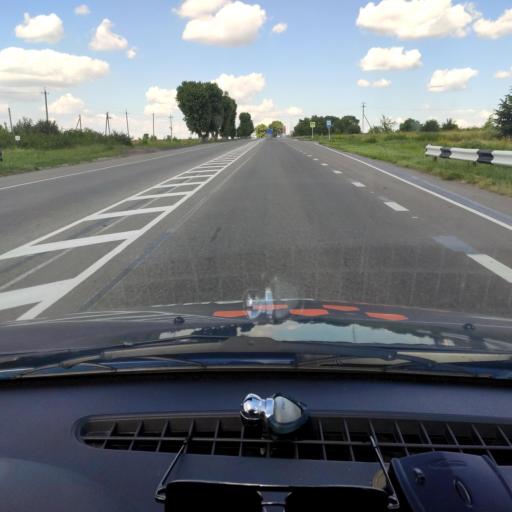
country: RU
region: Voronezj
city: Novovoronezh
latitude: 51.3393
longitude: 39.2715
